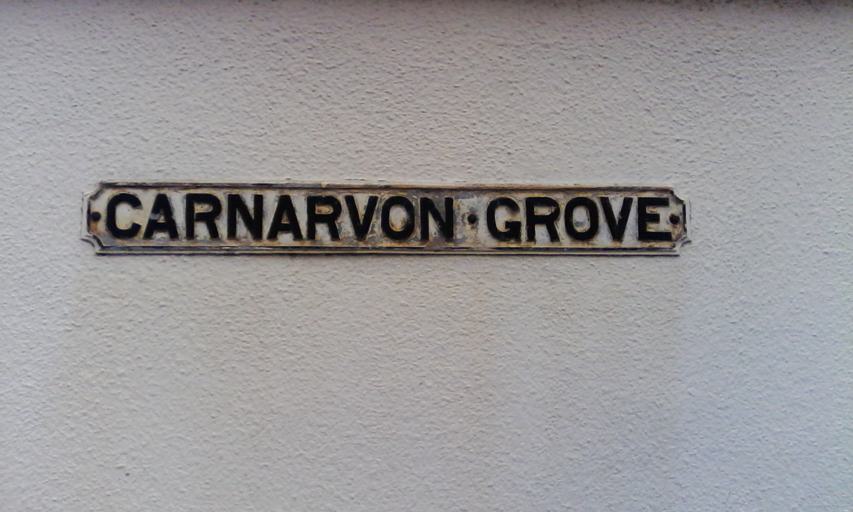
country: GB
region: England
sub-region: Nottinghamshire
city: Burton Joyce
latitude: 52.9756
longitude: -1.0797
